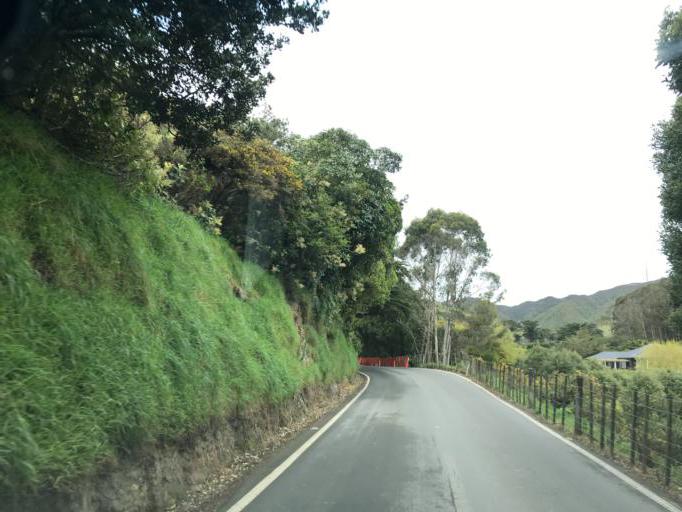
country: NZ
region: Wellington
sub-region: Wellington City
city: Kelburn
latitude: -41.2094
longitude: 174.7758
